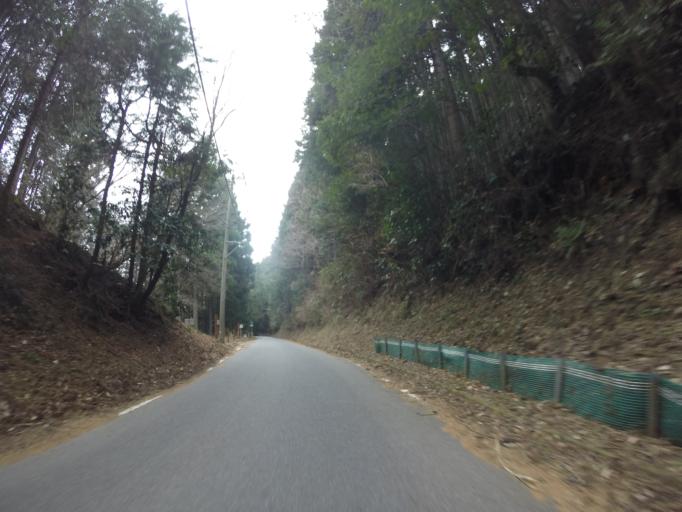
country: JP
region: Shizuoka
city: Fujinomiya
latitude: 35.2603
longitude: 138.5429
